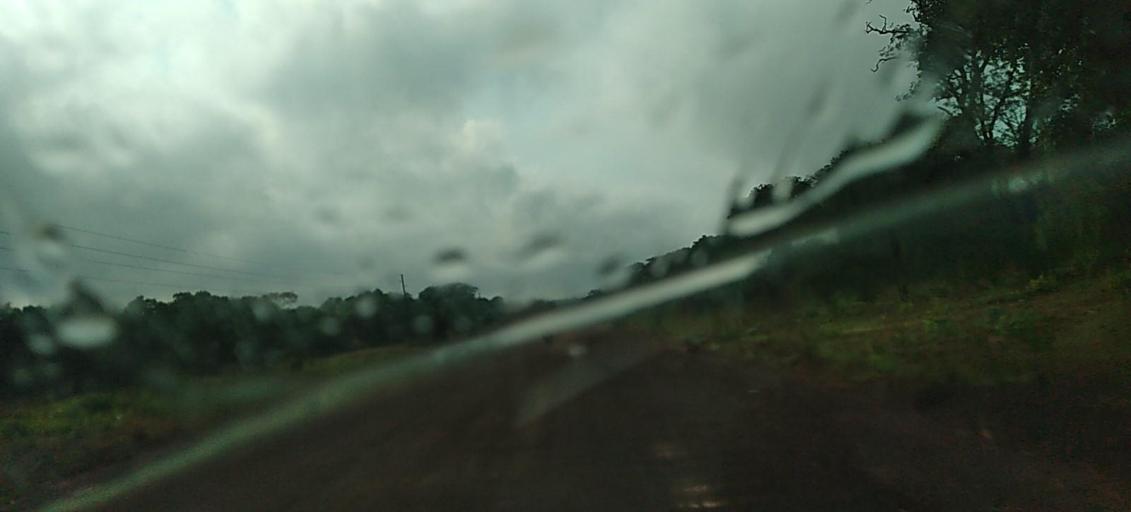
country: ZM
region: North-Western
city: Mwinilunga
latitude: -11.7282
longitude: 24.5791
